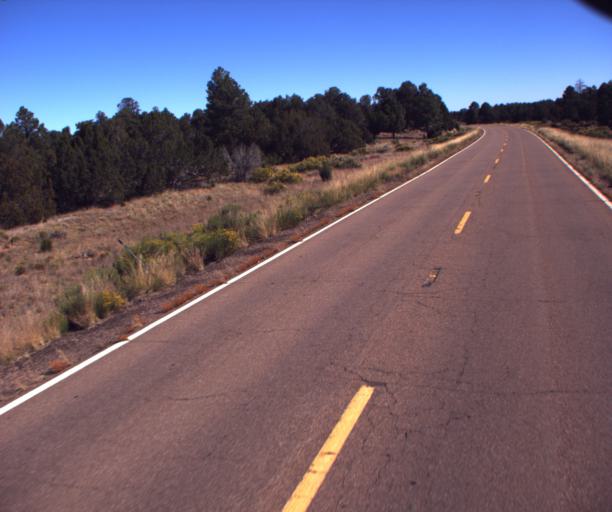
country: US
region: Arizona
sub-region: Navajo County
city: Heber-Overgaard
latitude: 34.4348
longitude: -110.5389
